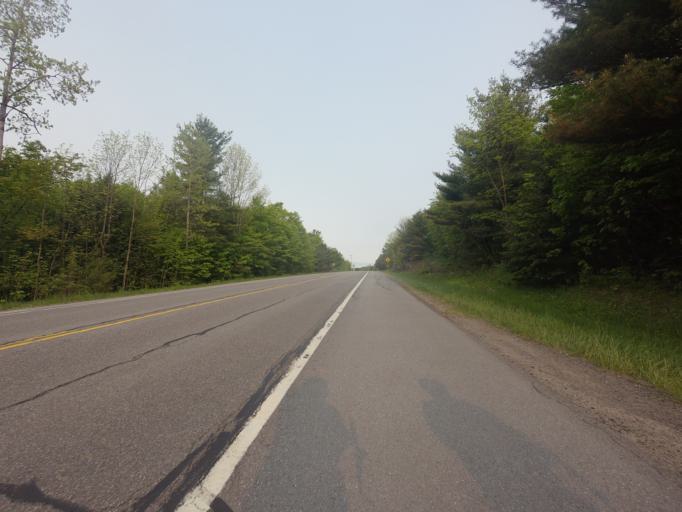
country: US
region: New York
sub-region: Jefferson County
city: Carthage
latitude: 44.0743
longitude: -75.4650
